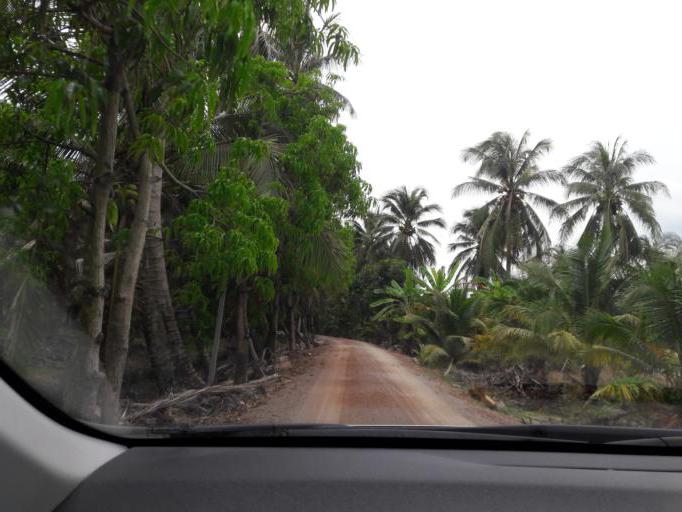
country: TH
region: Ratchaburi
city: Damnoen Saduak
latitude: 13.5549
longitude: 99.9932
